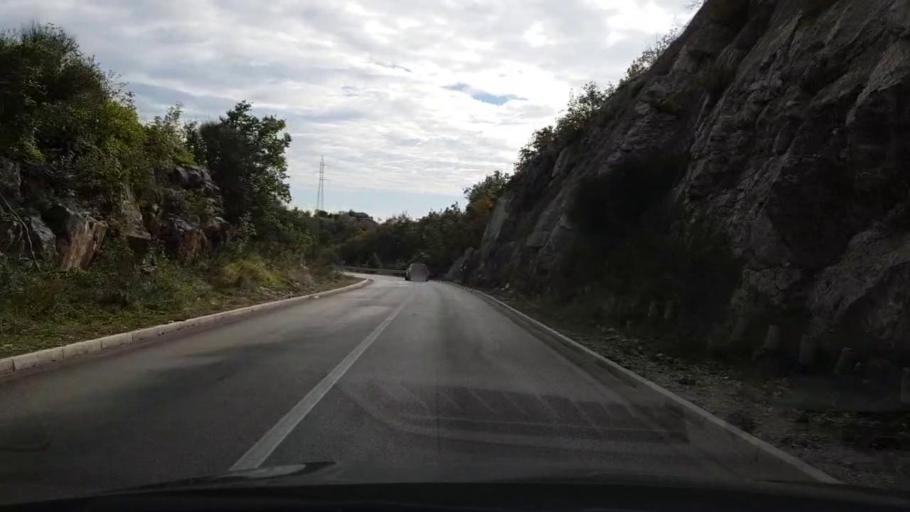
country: ME
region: Herceg Novi
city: Herceg-Novi
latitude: 42.4750
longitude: 18.5288
